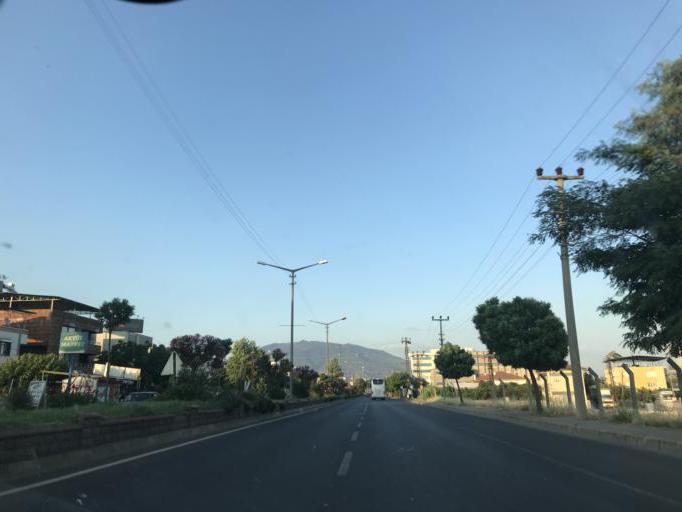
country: TR
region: Aydin
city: Nazilli
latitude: 37.9120
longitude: 28.3413
